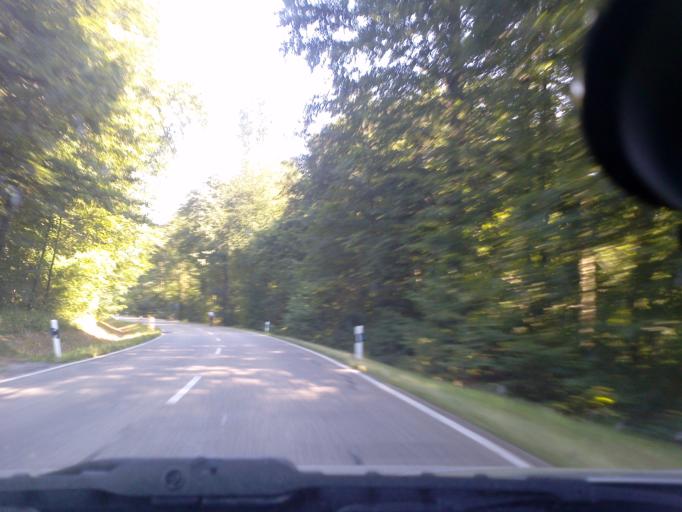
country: DE
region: Baden-Wuerttemberg
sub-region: Karlsruhe Region
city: Joehlingen
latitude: 49.0664
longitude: 8.6091
